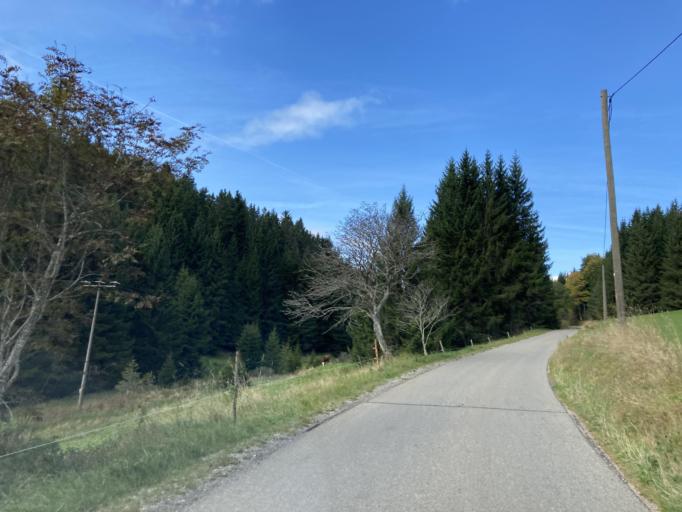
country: DE
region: Baden-Wuerttemberg
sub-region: Freiburg Region
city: Vohrenbach
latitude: 48.0673
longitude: 8.2828
